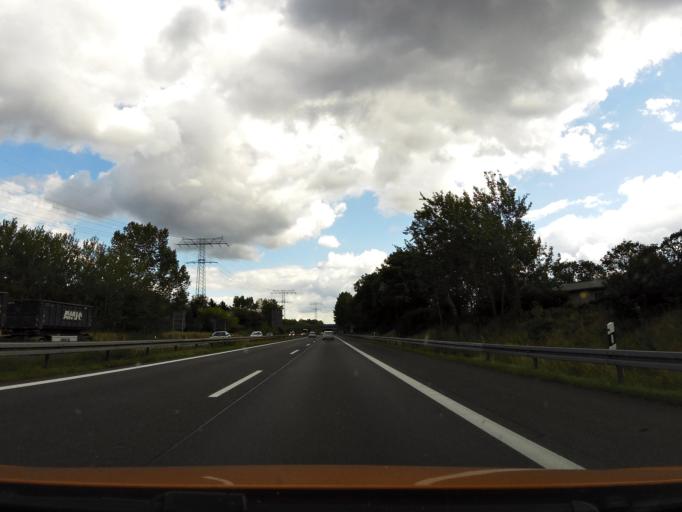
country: DE
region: Brandenburg
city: Birkenwerder
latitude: 52.6997
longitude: 13.2600
